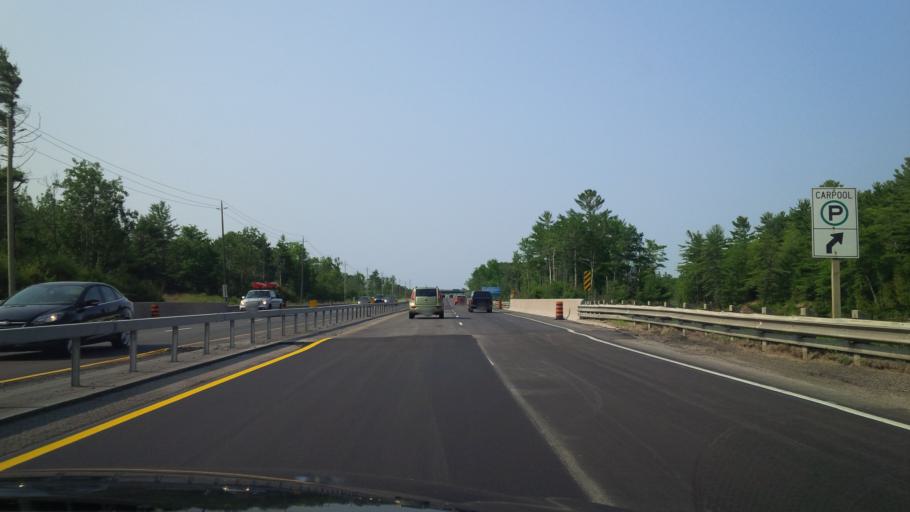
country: CA
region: Ontario
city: Gravenhurst
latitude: 44.7631
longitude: -79.3347
